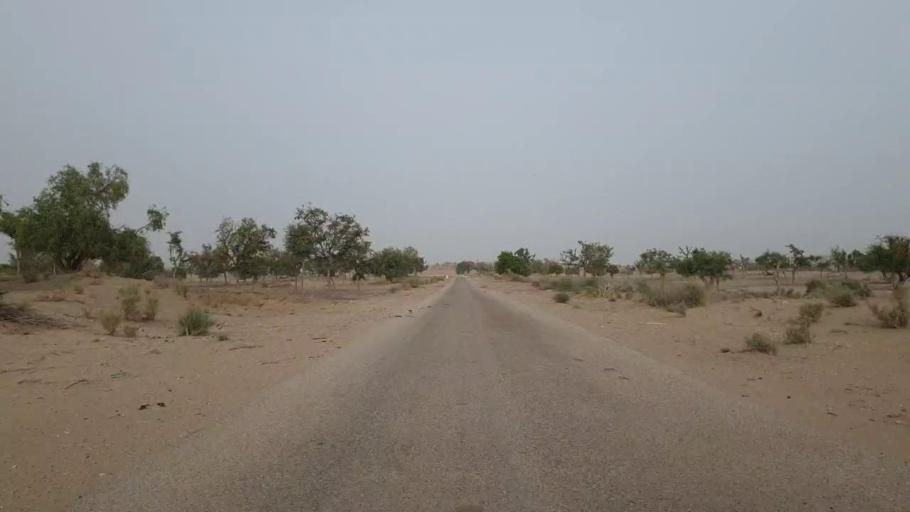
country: PK
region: Sindh
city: Islamkot
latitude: 24.5446
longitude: 70.3760
